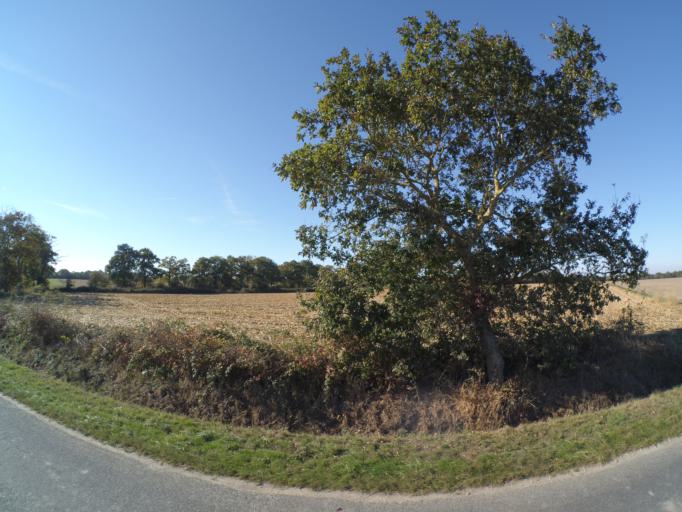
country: FR
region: Pays de la Loire
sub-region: Departement de la Loire-Atlantique
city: Saint-Lumine-de-Clisson
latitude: 47.0662
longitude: -1.3365
